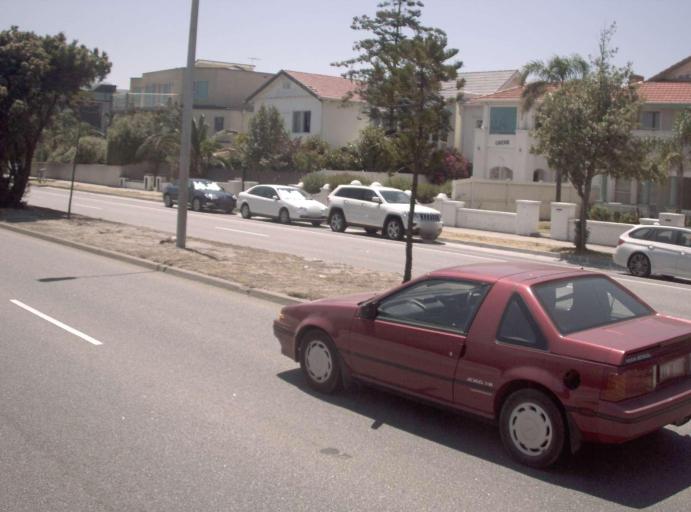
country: AU
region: Victoria
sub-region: Port Phillip
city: Elwood
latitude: -37.8796
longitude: 144.9773
